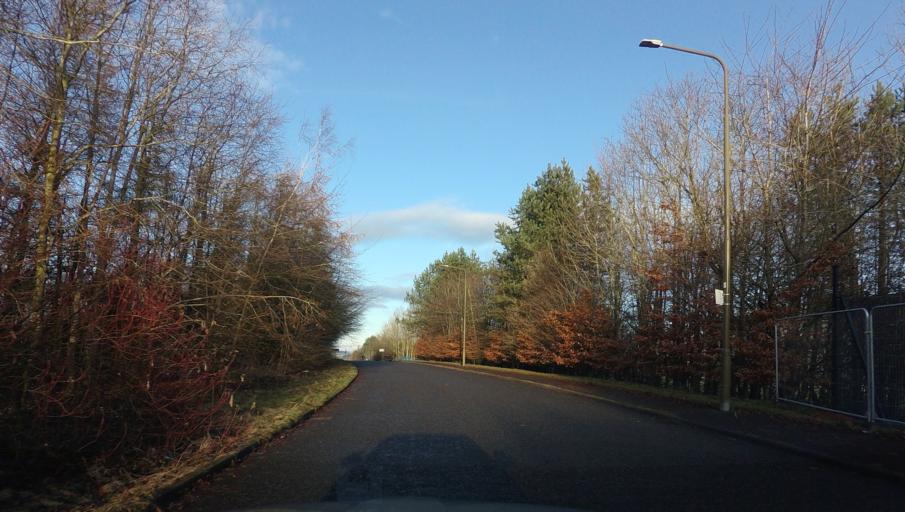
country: GB
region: Scotland
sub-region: West Lothian
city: Mid Calder
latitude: 55.8735
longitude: -3.4843
